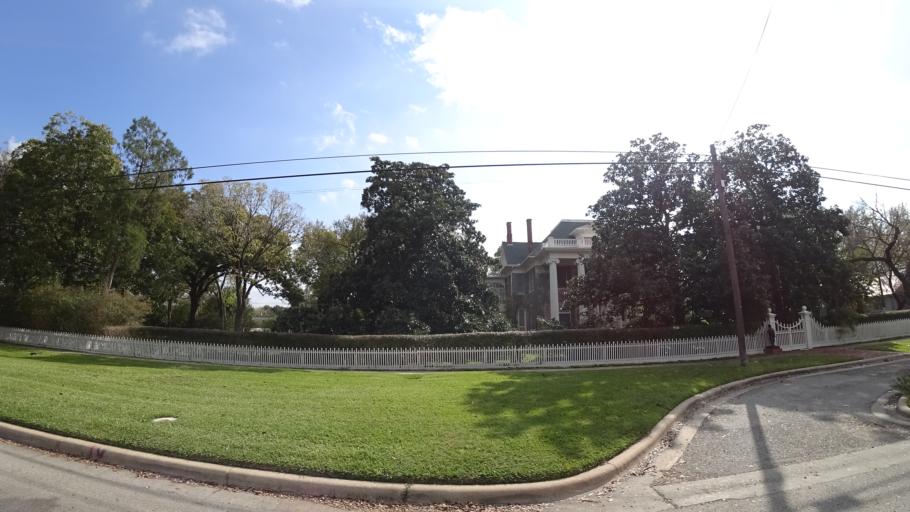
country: US
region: Texas
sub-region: Williamson County
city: Round Rock
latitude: 30.5096
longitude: -97.6752
